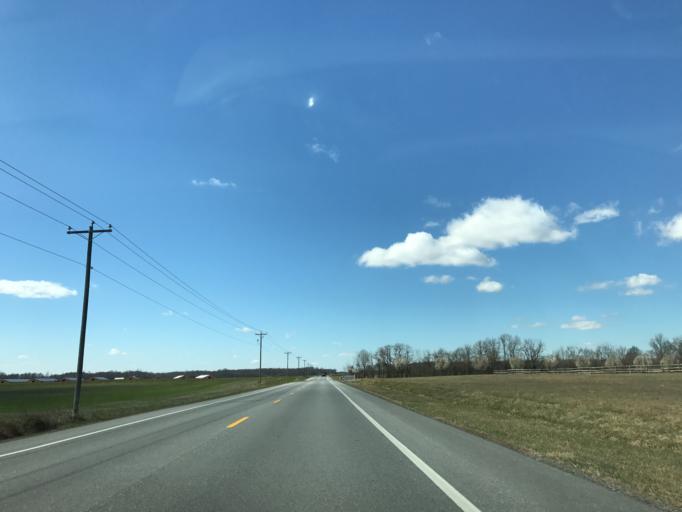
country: US
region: Maryland
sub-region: Queen Anne's County
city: Kingstown
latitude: 39.1195
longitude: -75.9276
